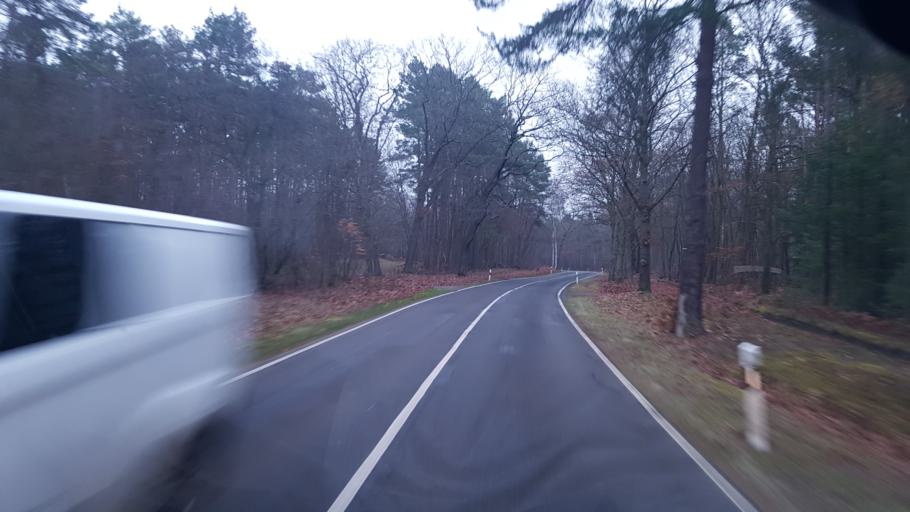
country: DE
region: Brandenburg
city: Drachhausen
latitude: 51.8800
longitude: 14.2953
